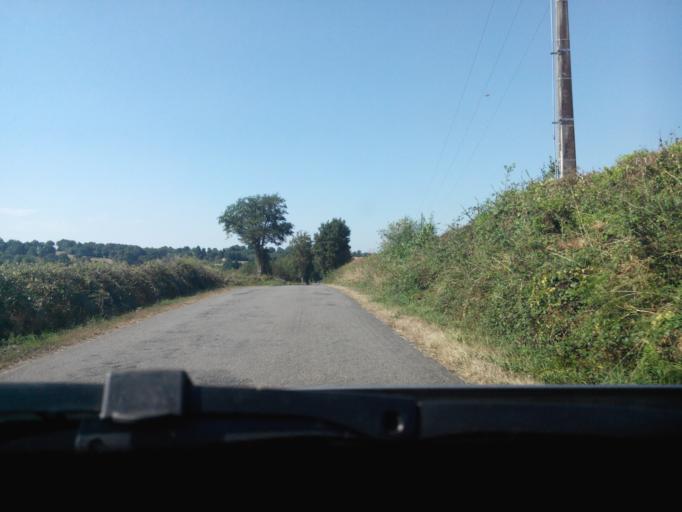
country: FR
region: Poitou-Charentes
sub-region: Departement de la Charente
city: Brigueuil
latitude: 45.9689
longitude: 0.7939
